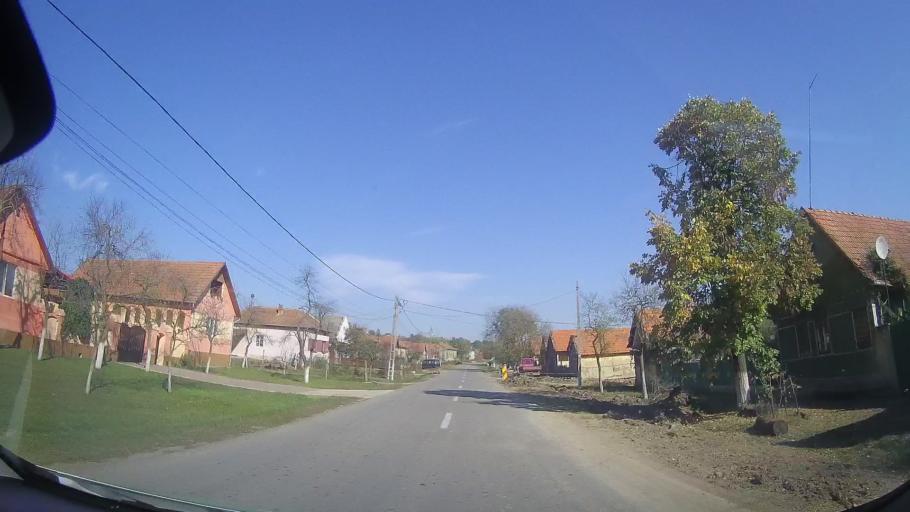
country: RO
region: Timis
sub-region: Comuna Secas
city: Secas
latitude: 45.8493
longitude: 21.7934
